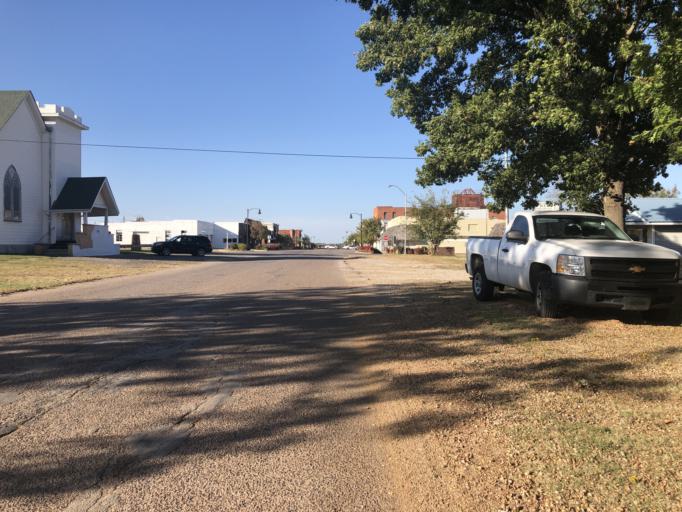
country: US
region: Oklahoma
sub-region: Pottawatomie County
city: Tecumseh
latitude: 35.2558
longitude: -96.9368
